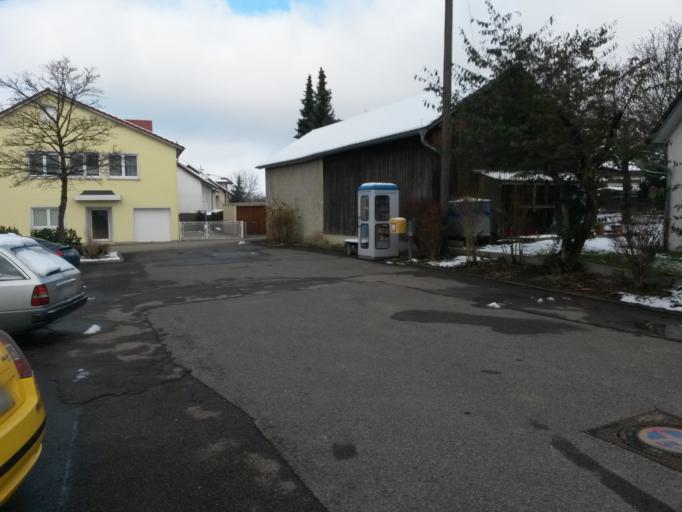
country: DE
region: Baden-Wuerttemberg
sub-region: Regierungsbezirk Stuttgart
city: Geislingen an der Steige
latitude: 48.6151
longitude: 9.8552
